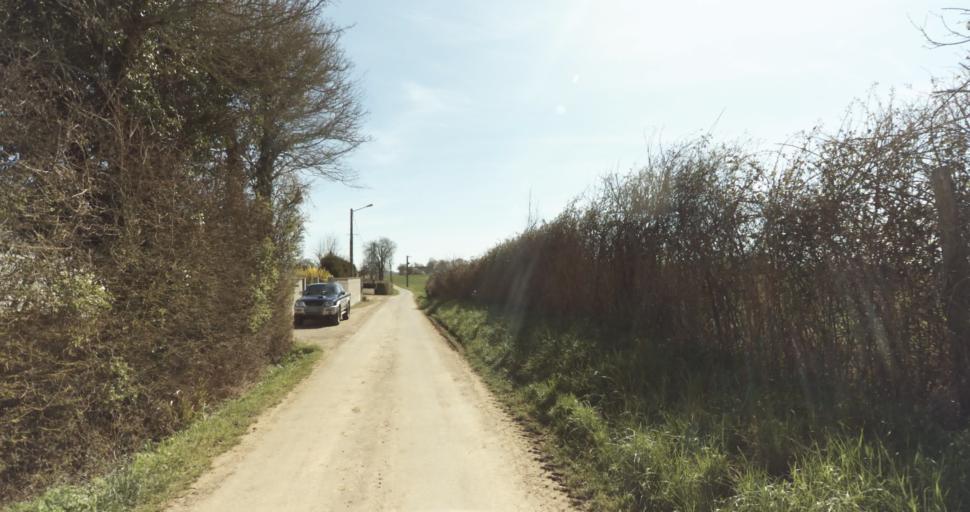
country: FR
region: Lower Normandy
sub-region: Departement du Calvados
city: Saint-Pierre-sur-Dives
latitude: 49.0569
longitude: -0.0146
